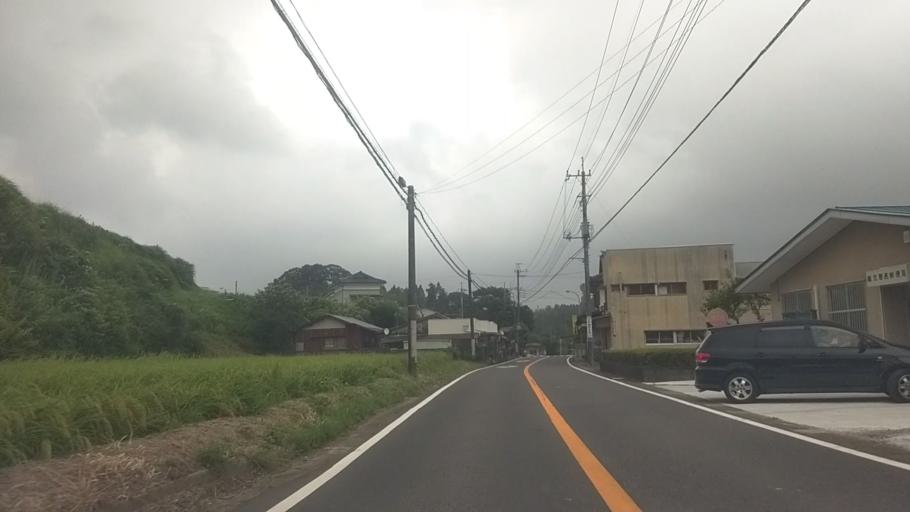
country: JP
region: Chiba
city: Katsuura
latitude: 35.2413
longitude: 140.2391
